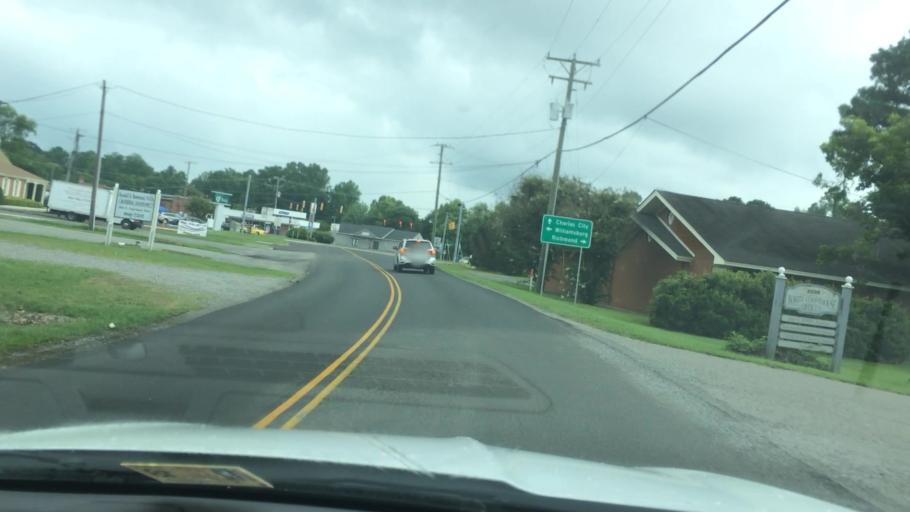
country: US
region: Virginia
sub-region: New Kent County
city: New Kent
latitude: 37.4437
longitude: -77.0445
